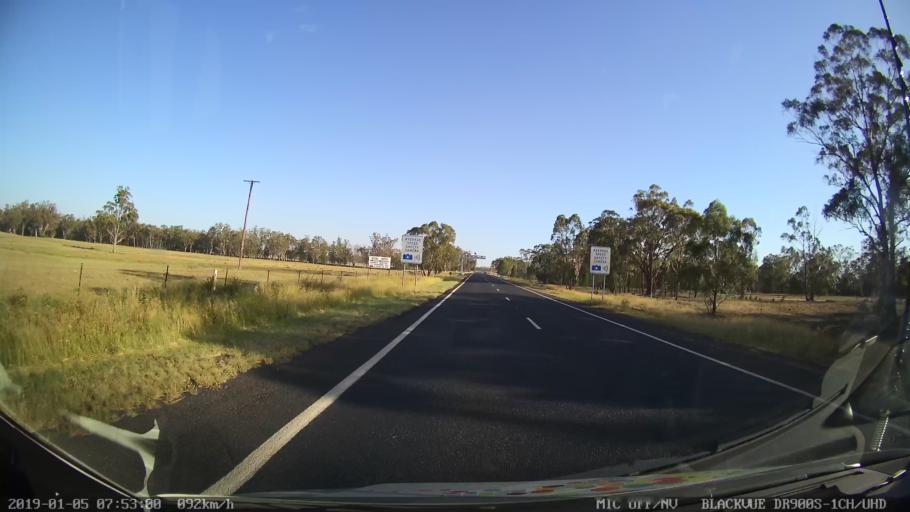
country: AU
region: New South Wales
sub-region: Gilgandra
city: Gilgandra
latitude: -31.7504
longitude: 148.6409
